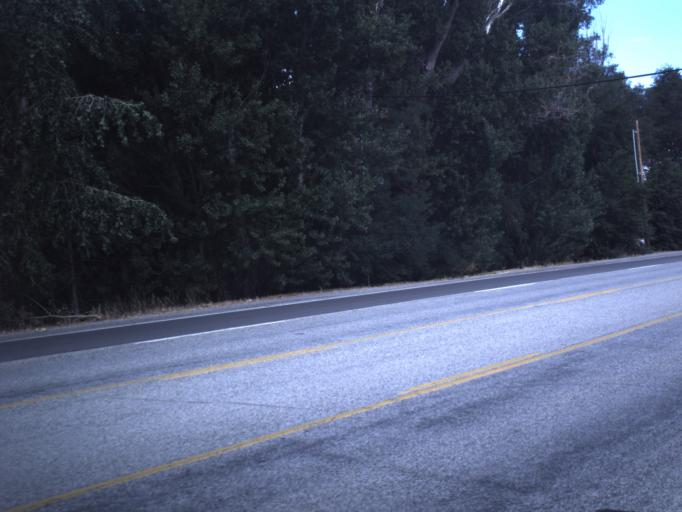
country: US
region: Utah
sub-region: Box Elder County
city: Willard
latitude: 41.4132
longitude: -112.0362
